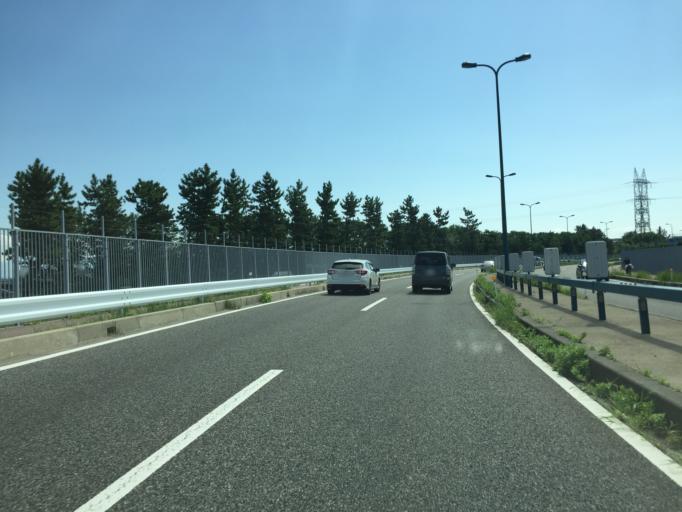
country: JP
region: Niigata
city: Niigata-shi
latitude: 37.9463
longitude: 139.0854
